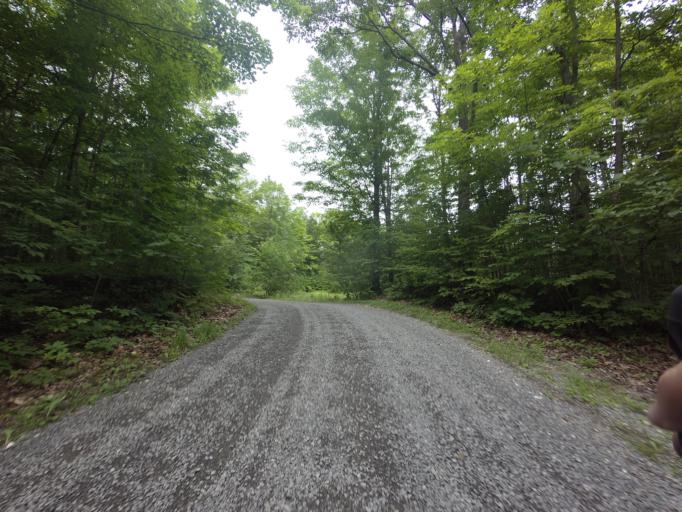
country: CA
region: Ontario
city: Kingston
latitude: 44.5629
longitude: -76.5719
